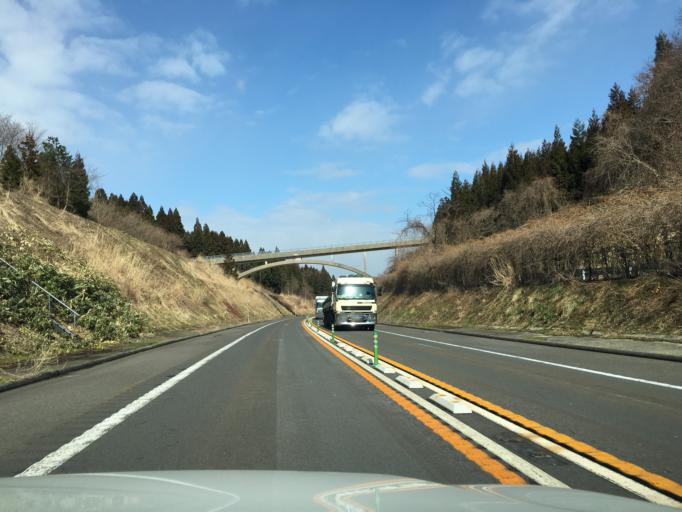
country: JP
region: Akita
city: Akita
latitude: 39.7668
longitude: 140.1230
